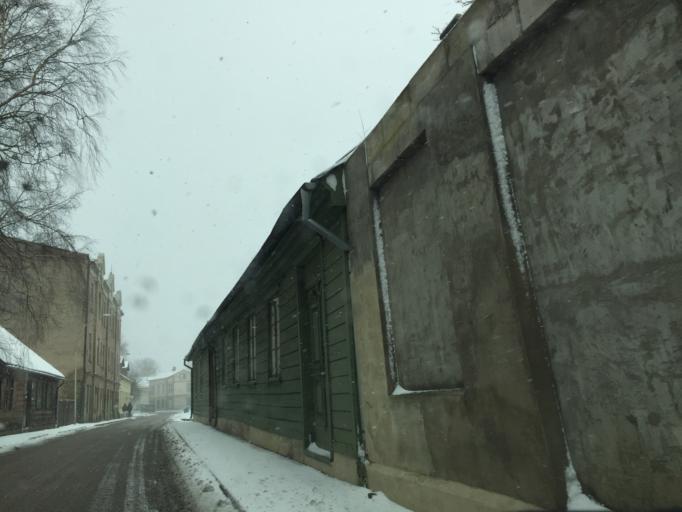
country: LV
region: Ventspils
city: Ventspils
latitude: 57.3953
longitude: 21.5563
